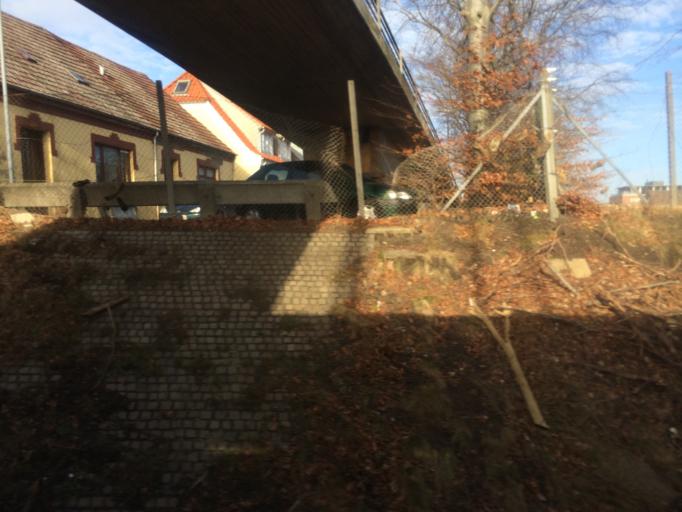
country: DK
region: Central Jutland
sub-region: Herning Kommune
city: Herning
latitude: 56.1334
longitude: 8.9632
